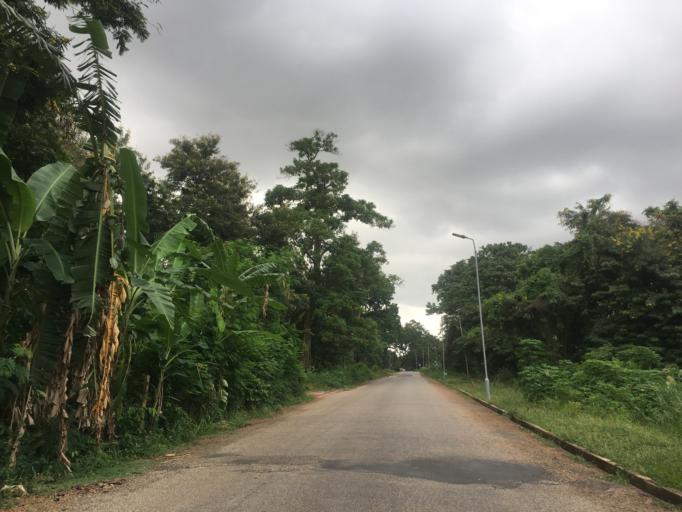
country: GH
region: Ashanti
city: Kumasi
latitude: 6.6712
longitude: -1.5869
